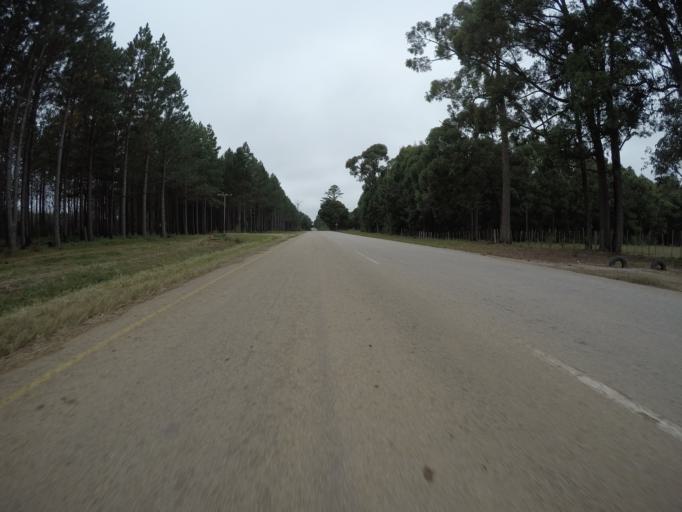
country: ZA
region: Eastern Cape
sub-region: Cacadu District Municipality
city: Kareedouw
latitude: -33.9913
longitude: 24.0868
